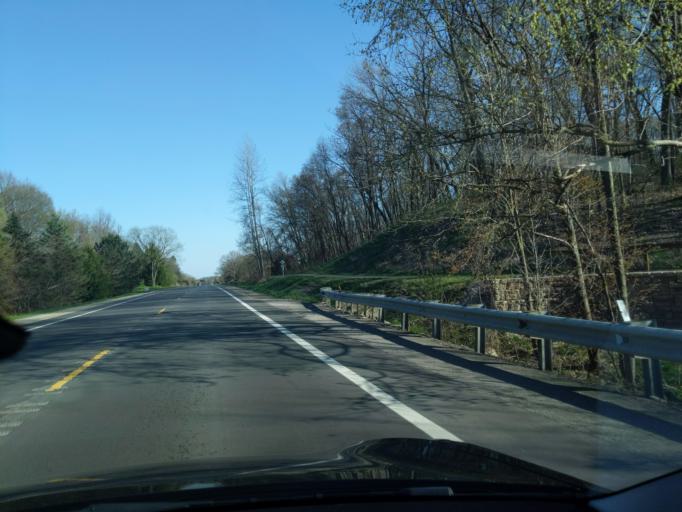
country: US
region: Michigan
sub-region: Washtenaw County
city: Chelsea
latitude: 42.3645
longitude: -84.0649
